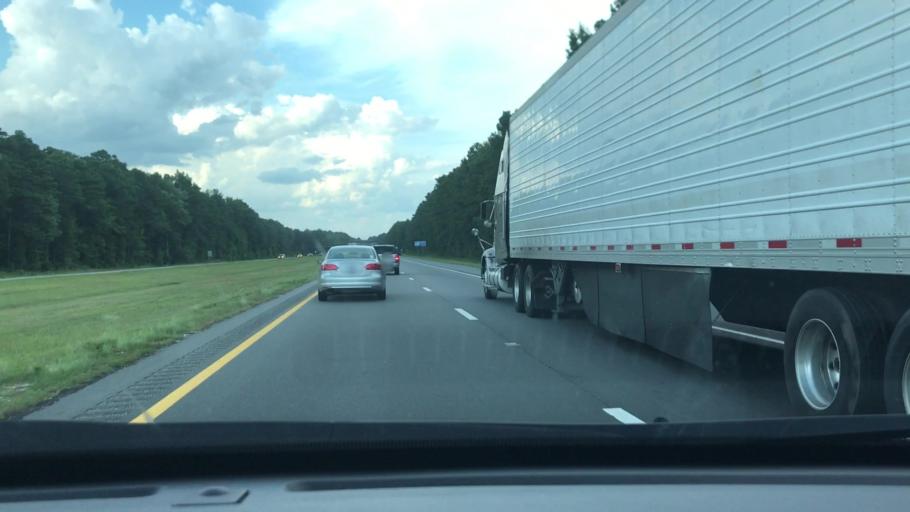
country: US
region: North Carolina
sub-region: Cumberland County
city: Hope Mills
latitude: 34.9513
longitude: -78.9016
